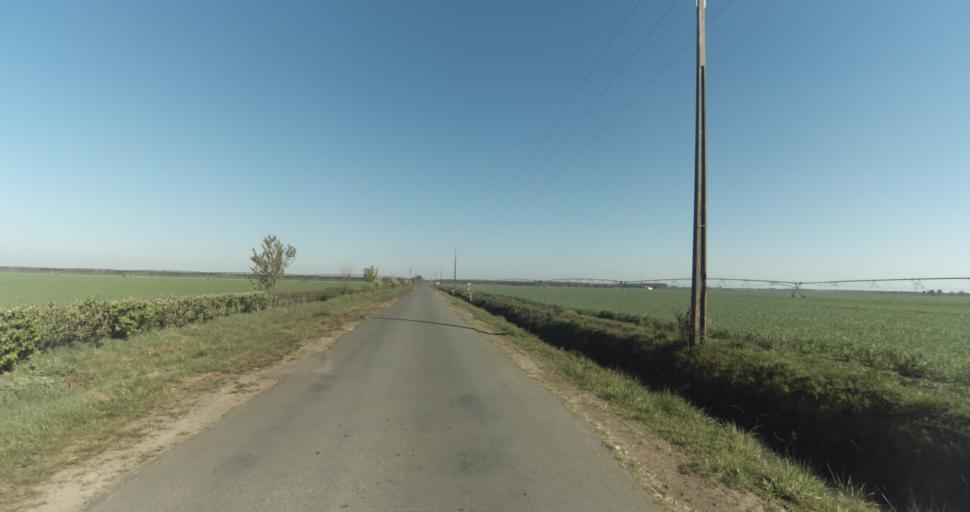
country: FR
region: Aquitaine
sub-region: Departement de la Gironde
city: Marcheprime
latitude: 44.7665
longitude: -0.8549
